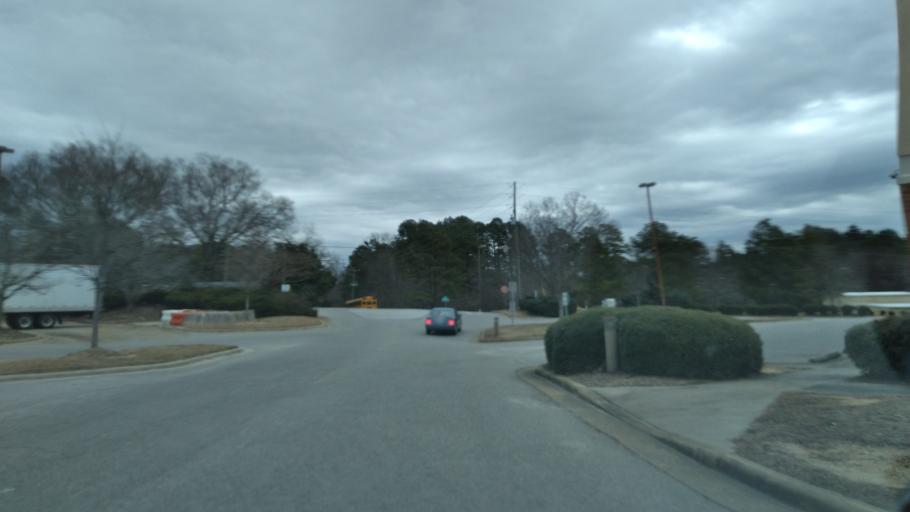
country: US
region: North Carolina
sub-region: Wake County
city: Garner
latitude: 35.7135
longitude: -78.6350
